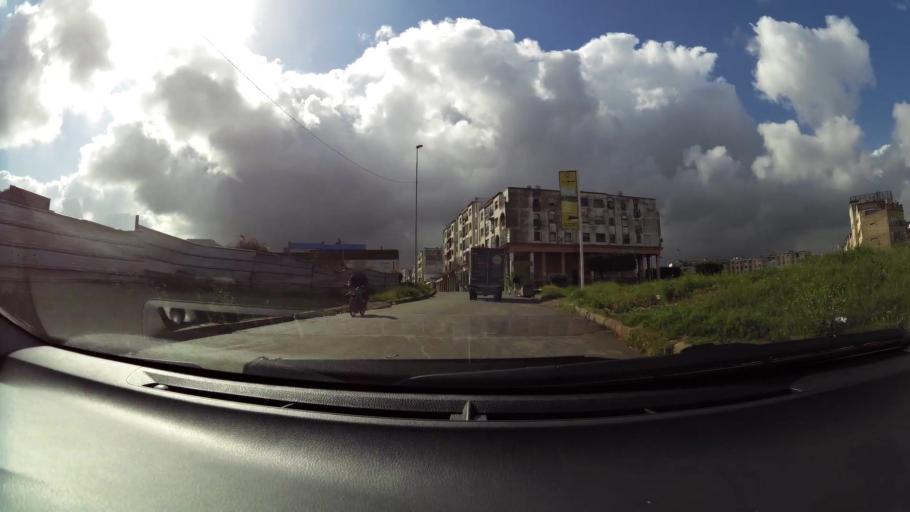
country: MA
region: Grand Casablanca
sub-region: Mediouna
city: Tit Mellil
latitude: 33.5760
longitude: -7.5302
